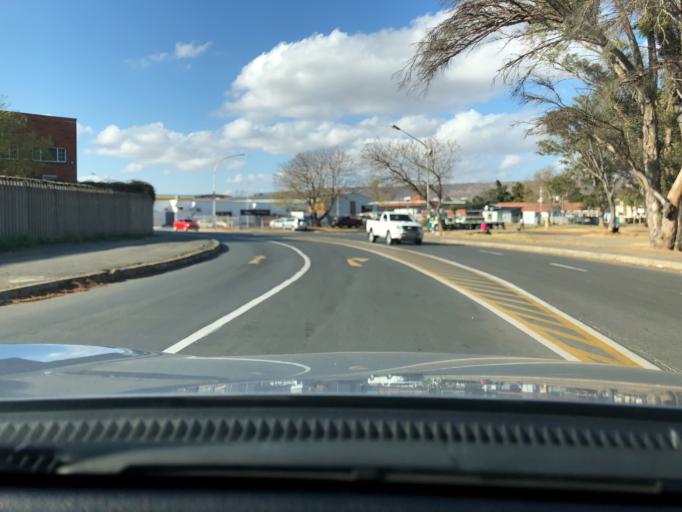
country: ZA
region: KwaZulu-Natal
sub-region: uThukela District Municipality
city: Ladysmith
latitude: -28.5608
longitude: 29.7778
